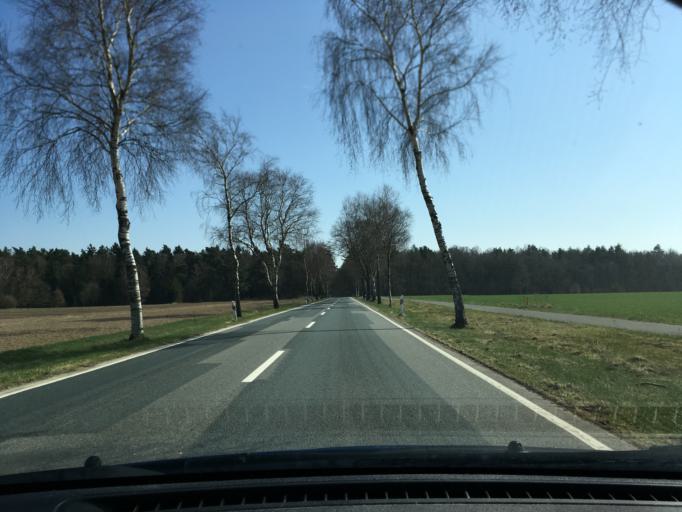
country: DE
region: Lower Saxony
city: Rehlingen
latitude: 53.0932
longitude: 10.2649
